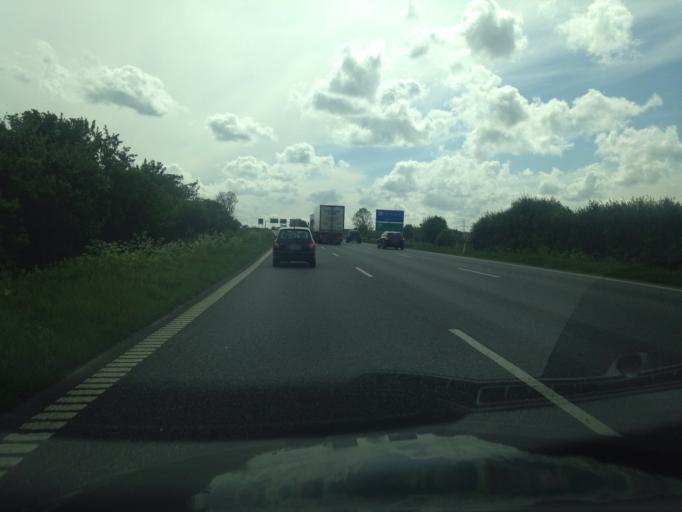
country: DK
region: South Denmark
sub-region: Kolding Kommune
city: Kolding
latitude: 55.5434
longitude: 9.5176
